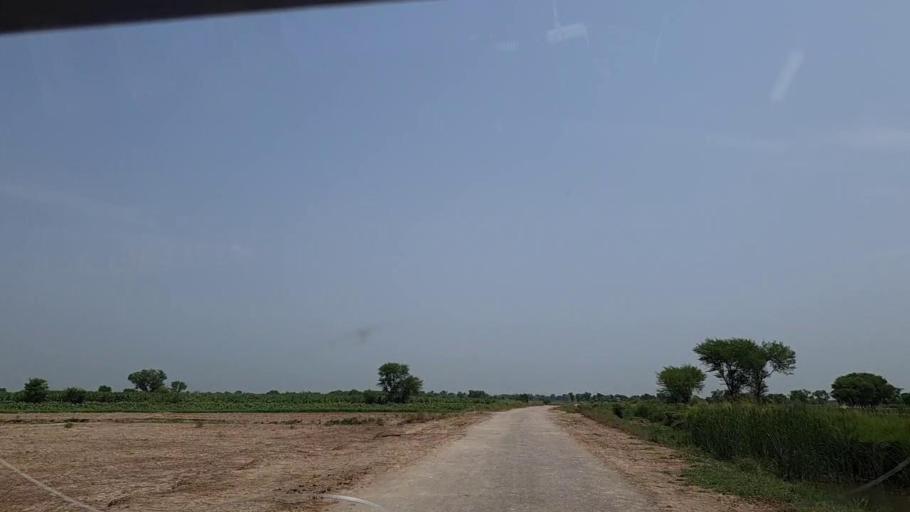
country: PK
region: Sindh
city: Tharu Shah
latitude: 26.9001
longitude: 68.0521
